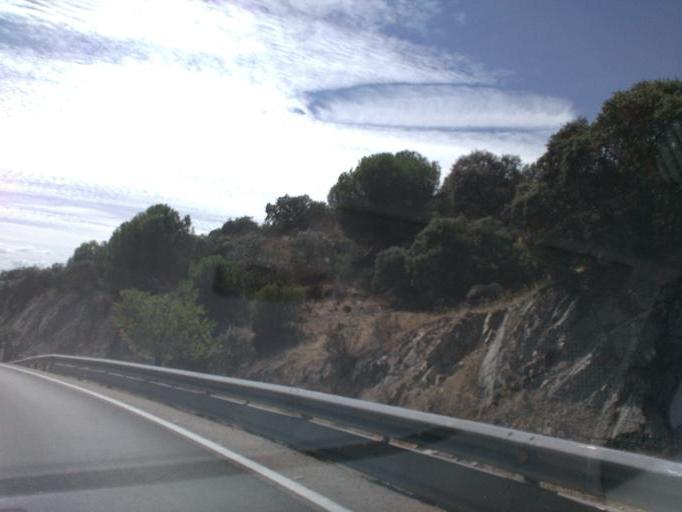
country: ES
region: Madrid
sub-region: Provincia de Madrid
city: Torrelodones
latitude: 40.5459
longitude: -3.9596
